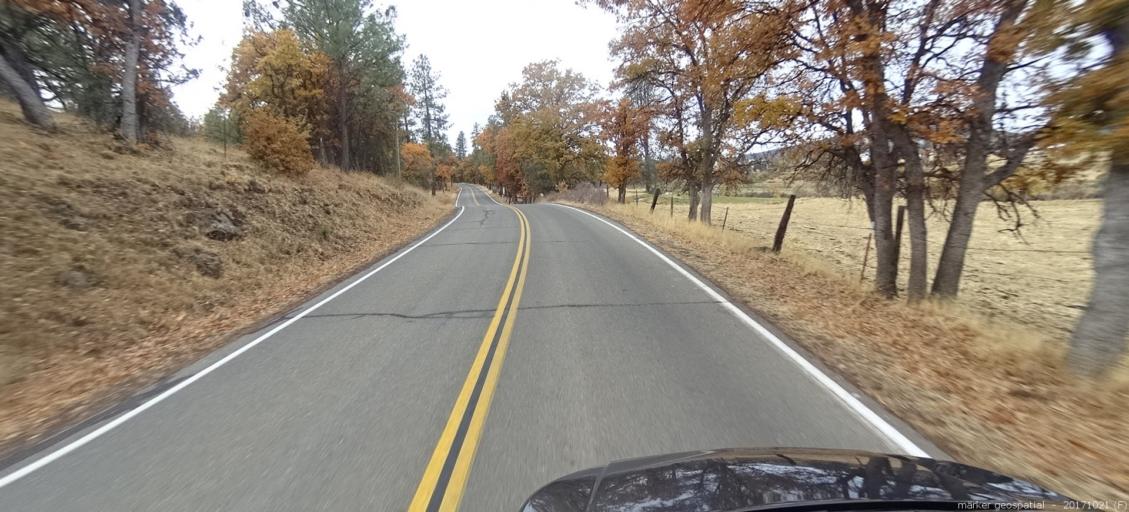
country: US
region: California
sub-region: Shasta County
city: Burney
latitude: 41.0062
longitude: -121.4285
